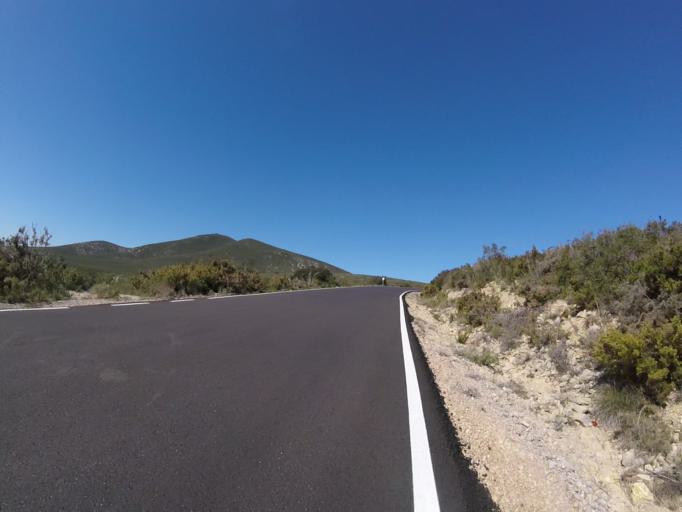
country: ES
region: Valencia
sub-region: Provincia de Castello
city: Cervera del Maestre
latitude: 40.4009
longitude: 0.2323
